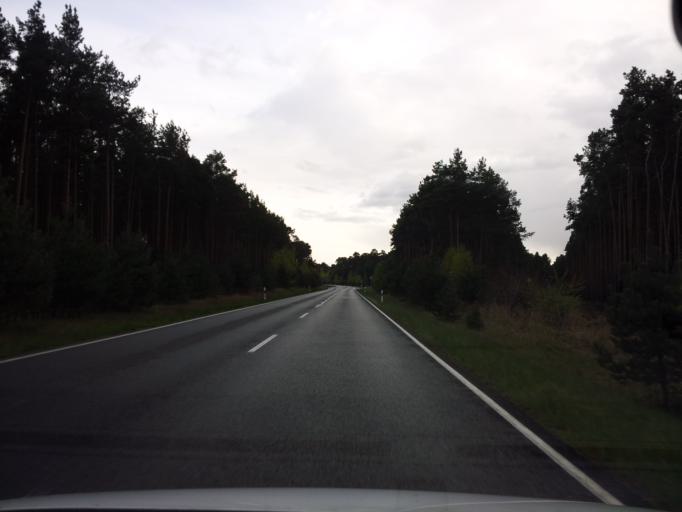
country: DE
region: Brandenburg
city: Janschwalde
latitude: 51.8499
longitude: 14.5145
